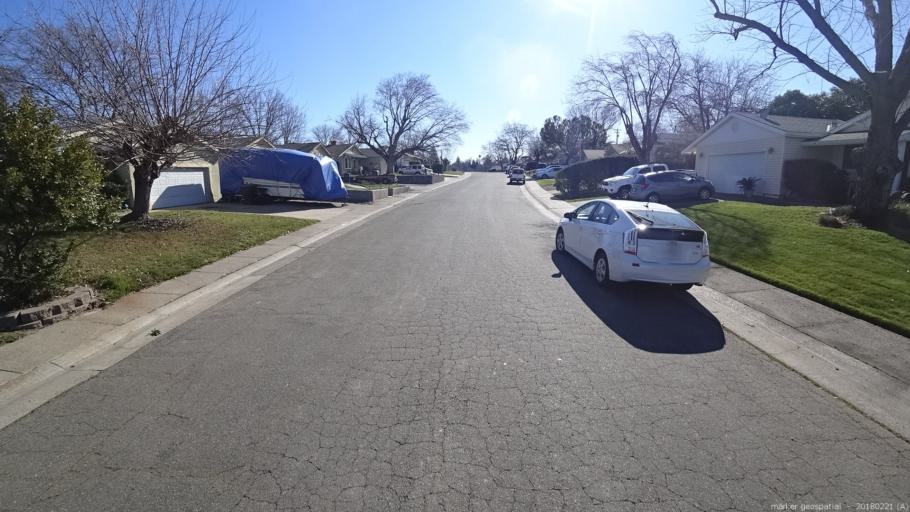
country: US
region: California
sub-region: Sacramento County
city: Orangevale
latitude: 38.6886
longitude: -121.2433
